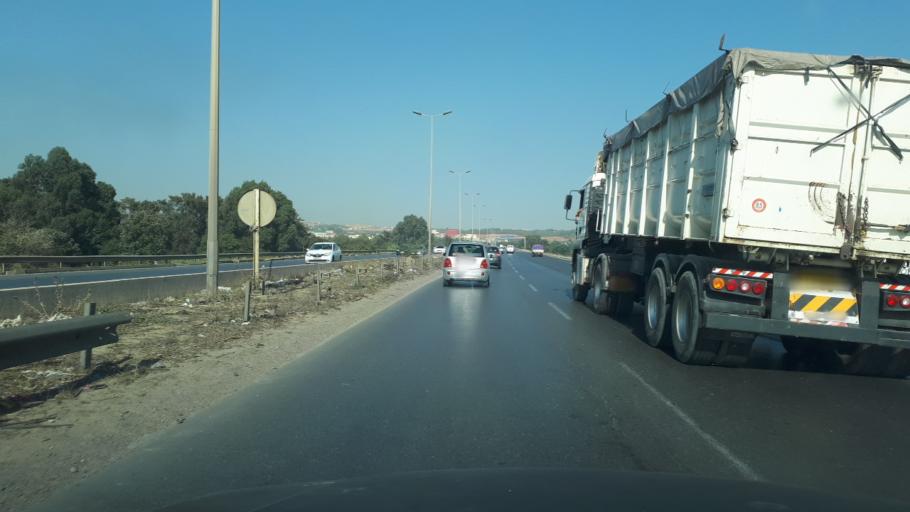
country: DZ
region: Tipaza
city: Baraki
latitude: 36.6766
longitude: 3.0717
